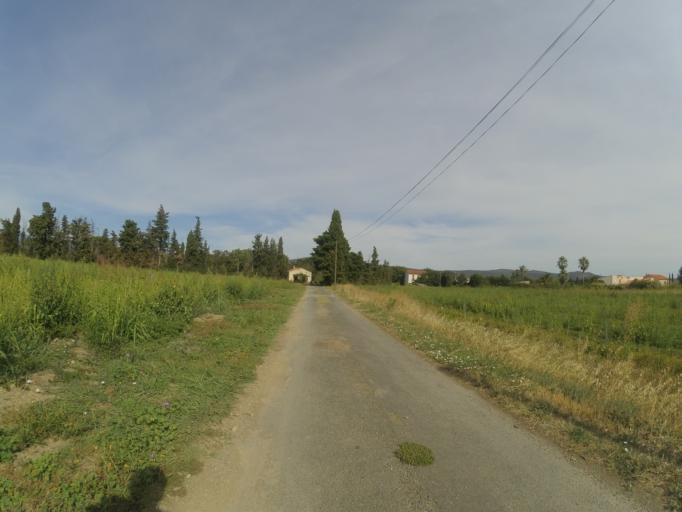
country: FR
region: Languedoc-Roussillon
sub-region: Departement des Pyrenees-Orientales
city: Ille-sur-Tet
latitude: 42.6608
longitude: 2.6266
